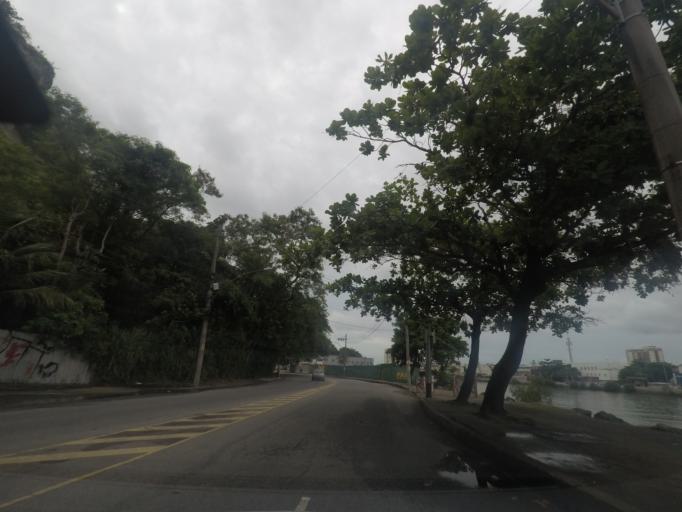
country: BR
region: Rio de Janeiro
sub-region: Rio De Janeiro
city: Rio de Janeiro
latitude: -23.0074
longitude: -43.3027
